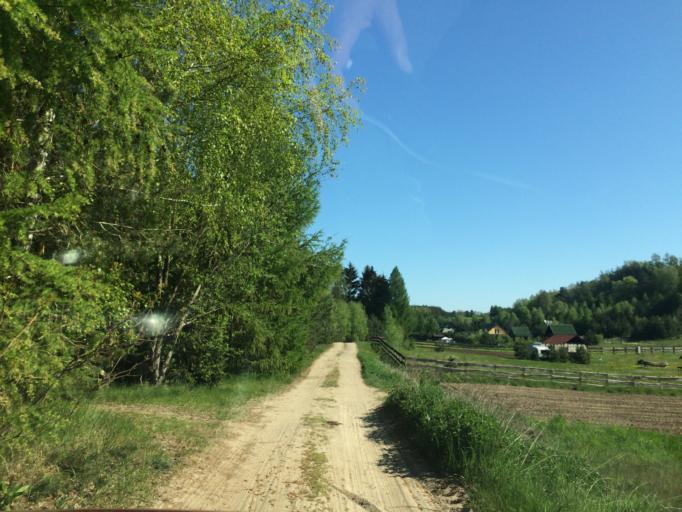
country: PL
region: Warmian-Masurian Voivodeship
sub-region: Powiat nowomiejski
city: Biskupiec
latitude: 53.4898
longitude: 19.4760
